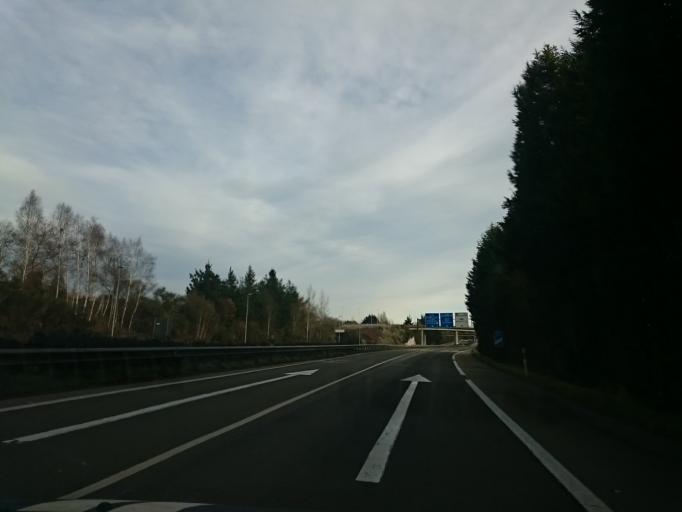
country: ES
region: Asturias
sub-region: Province of Asturias
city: Oviedo
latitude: 43.3409
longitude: -5.8679
